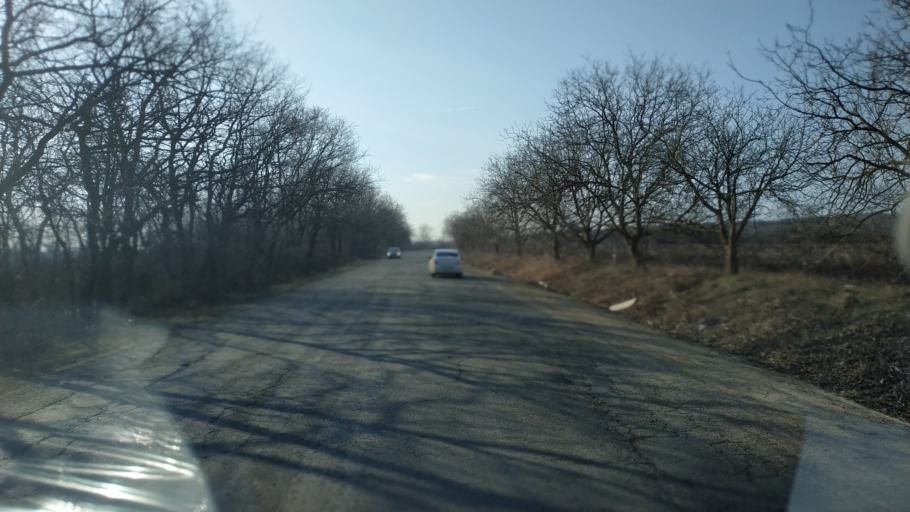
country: MD
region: Chisinau
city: Singera
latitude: 46.8702
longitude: 29.0398
